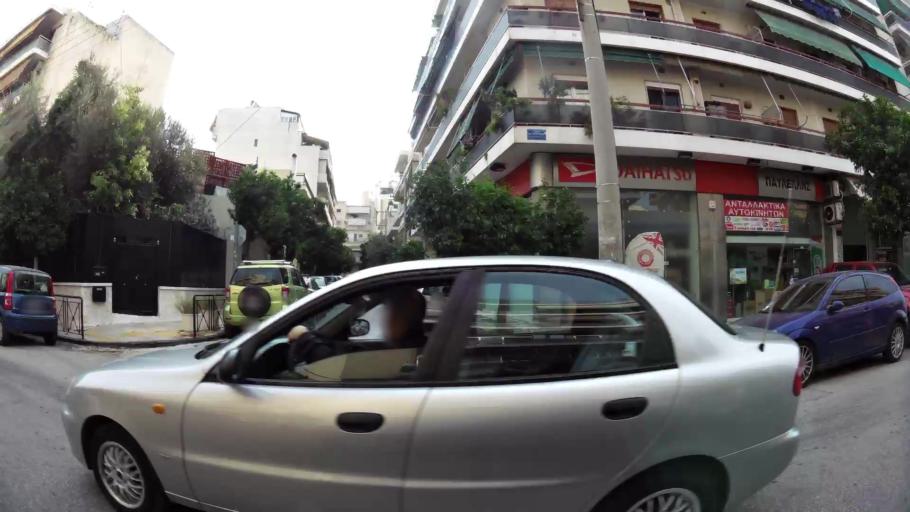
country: GR
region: Attica
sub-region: Nomarchia Athinas
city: Nea Chalkidona
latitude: 38.0170
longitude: 23.7238
